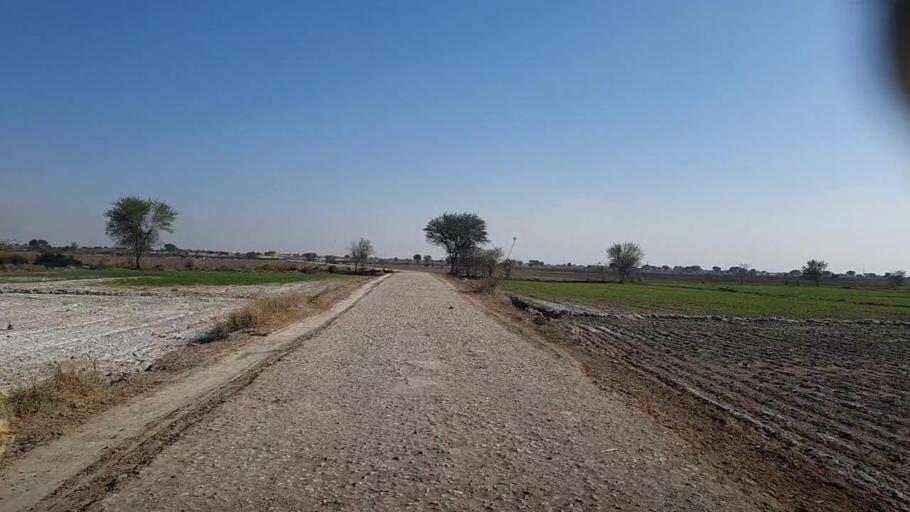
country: PK
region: Sindh
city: Khairpur
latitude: 27.9272
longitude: 69.7332
